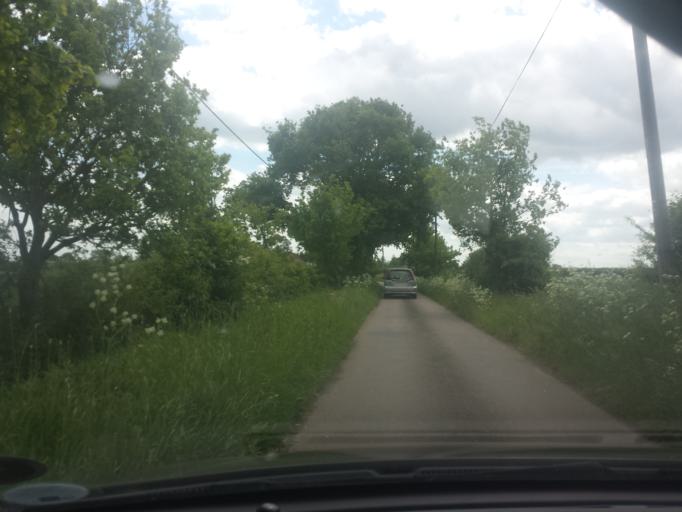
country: GB
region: England
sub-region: Essex
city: Little Clacton
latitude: 51.8656
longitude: 1.1384
